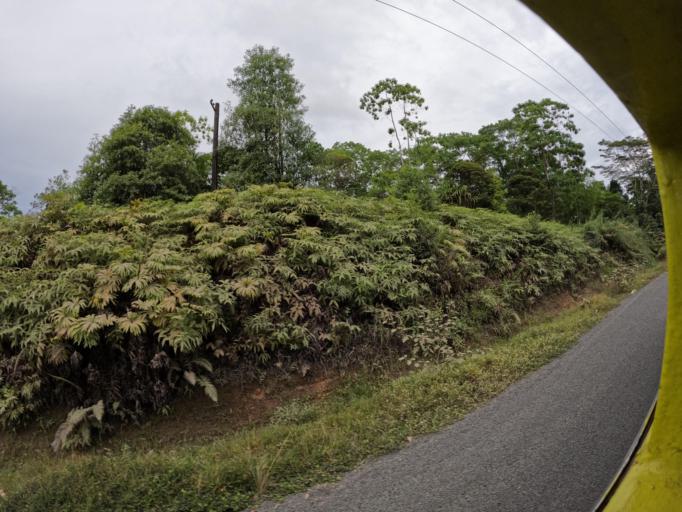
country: FJ
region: Central
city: Suva
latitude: -18.0654
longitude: 178.4589
